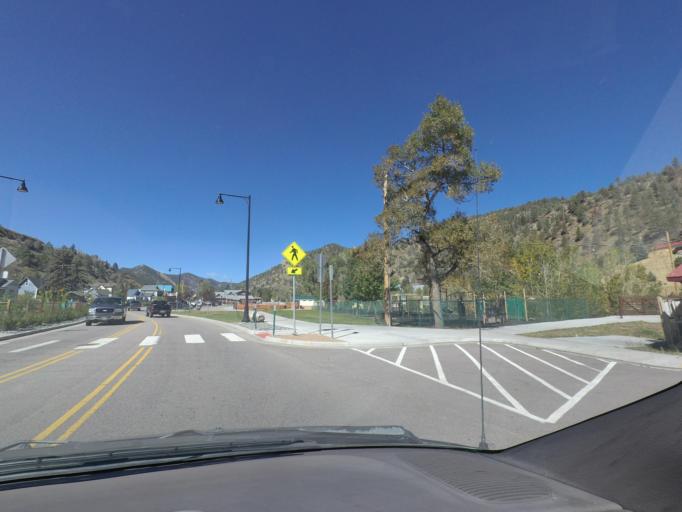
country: US
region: Colorado
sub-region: Clear Creek County
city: Idaho Springs
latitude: 39.7419
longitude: -105.5069
